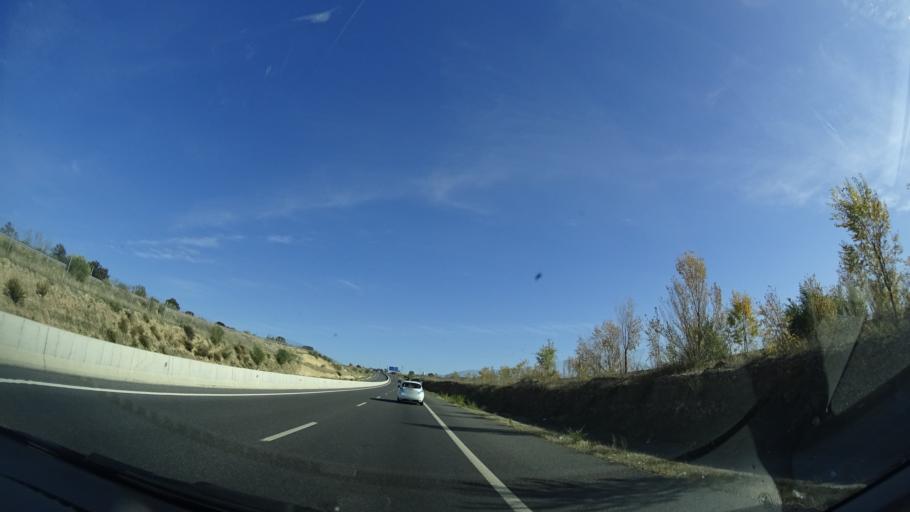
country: ES
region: Madrid
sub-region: Provincia de Madrid
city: Las Rozas de Madrid
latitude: 40.4799
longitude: -3.9074
